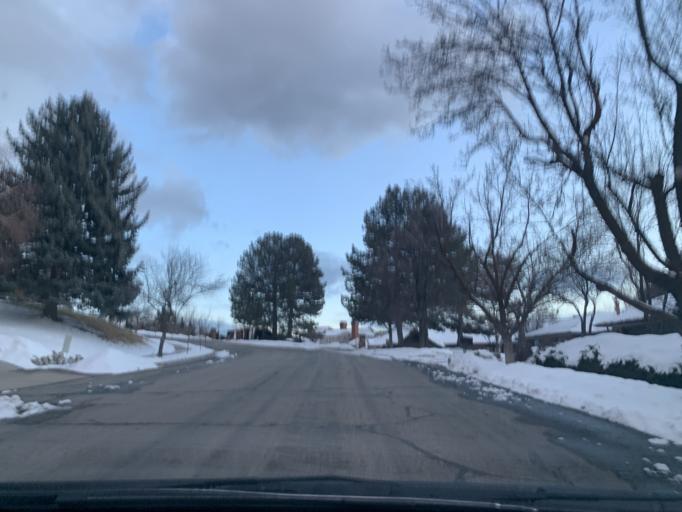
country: US
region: Utah
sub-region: Salt Lake County
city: Salt Lake City
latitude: 40.7808
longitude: -111.8431
